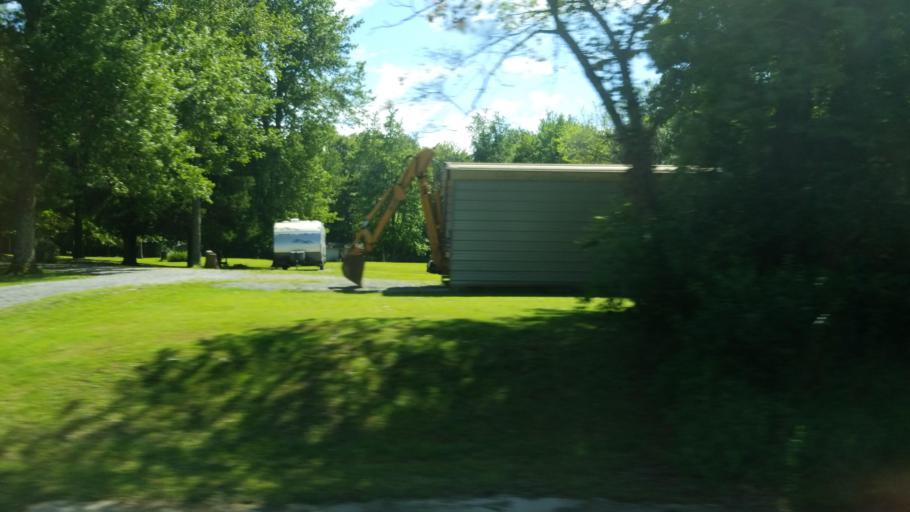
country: US
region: Illinois
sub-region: Williamson County
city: Johnston City
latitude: 37.7892
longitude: -88.9088
